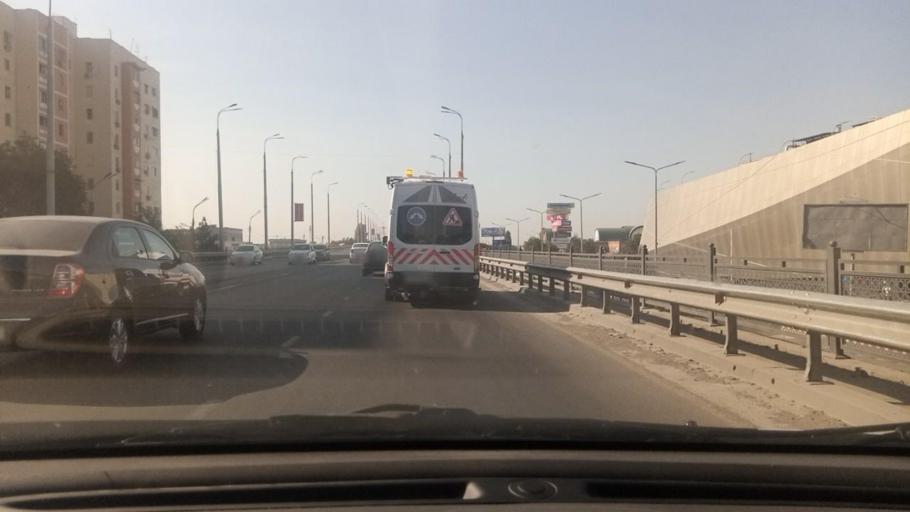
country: UZ
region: Toshkent Shahri
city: Bektemir
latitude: 41.2404
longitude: 69.3294
